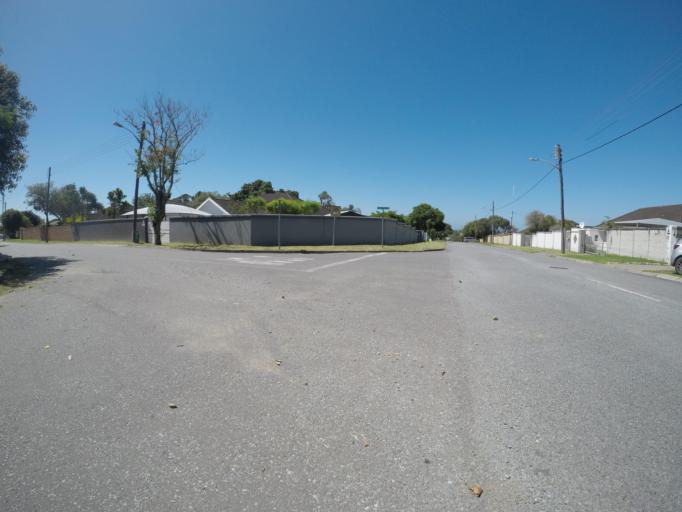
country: ZA
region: Eastern Cape
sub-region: Buffalo City Metropolitan Municipality
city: East London
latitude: -32.9674
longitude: 27.9427
